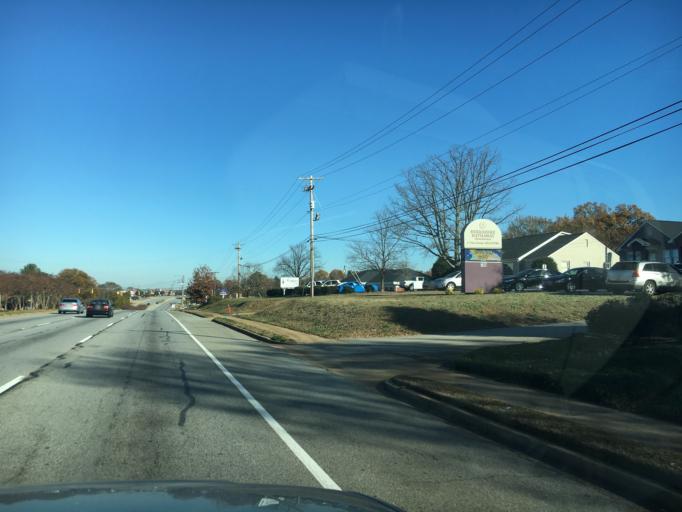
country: US
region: South Carolina
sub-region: Greenville County
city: Greer
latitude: 34.9463
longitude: -82.2463
